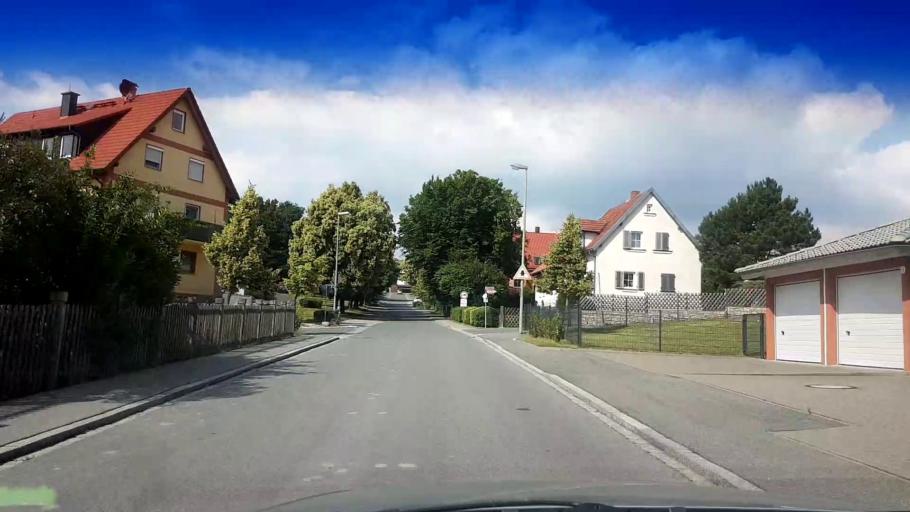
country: DE
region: Bavaria
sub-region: Upper Franconia
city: Priesendorf
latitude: 49.8960
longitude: 10.7272
